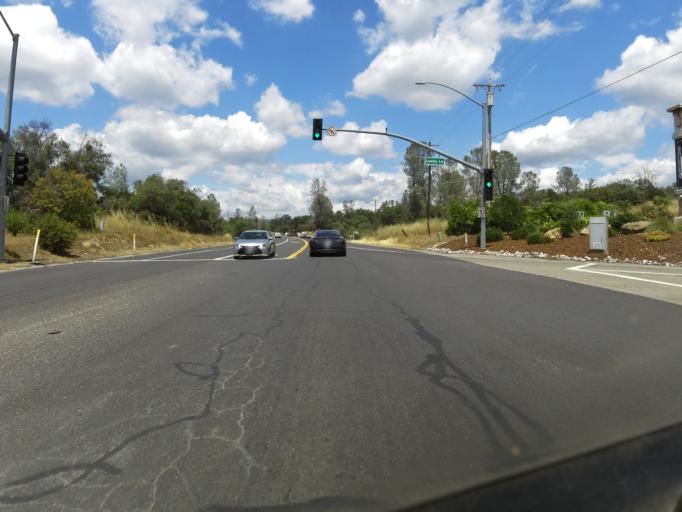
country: US
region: California
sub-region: Madera County
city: Coarsegold
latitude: 37.2135
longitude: -119.7086
